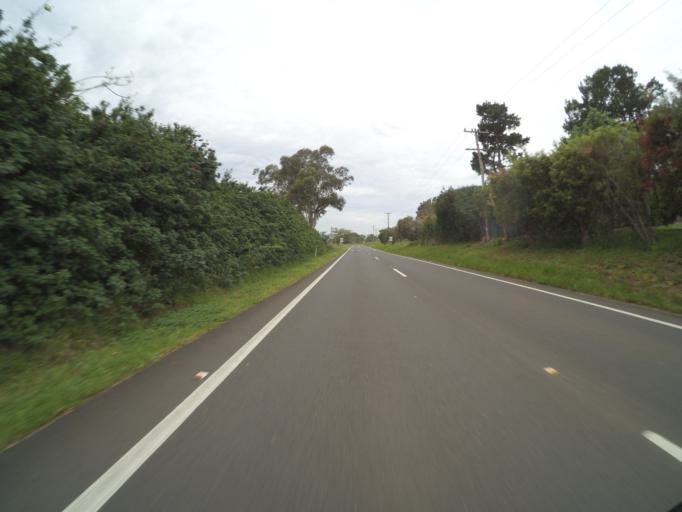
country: AU
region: New South Wales
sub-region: Kiama
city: Jamberoo
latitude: -34.6490
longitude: 150.7850
